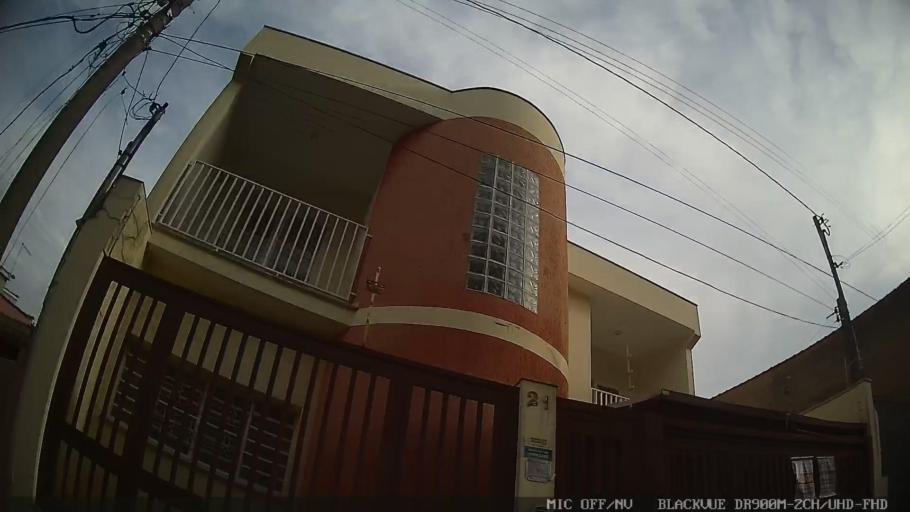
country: BR
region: Sao Paulo
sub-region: Braganca Paulista
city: Braganca Paulista
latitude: -22.9486
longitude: -46.5457
